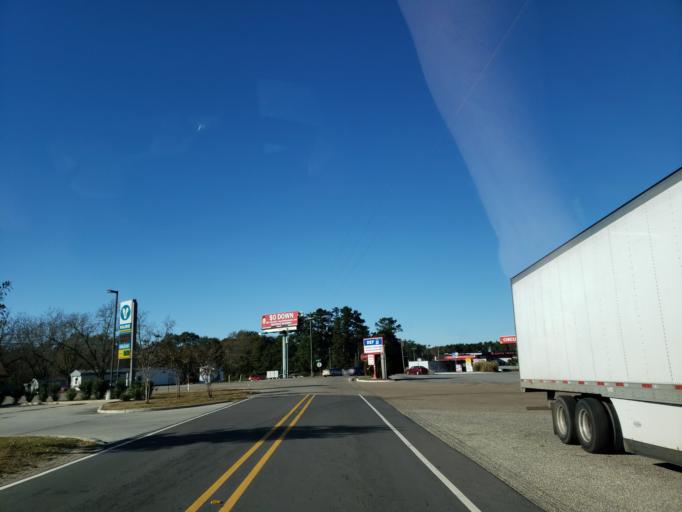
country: US
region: Mississippi
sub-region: Lamar County
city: West Hattiesburg
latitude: 31.2560
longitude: -89.3386
